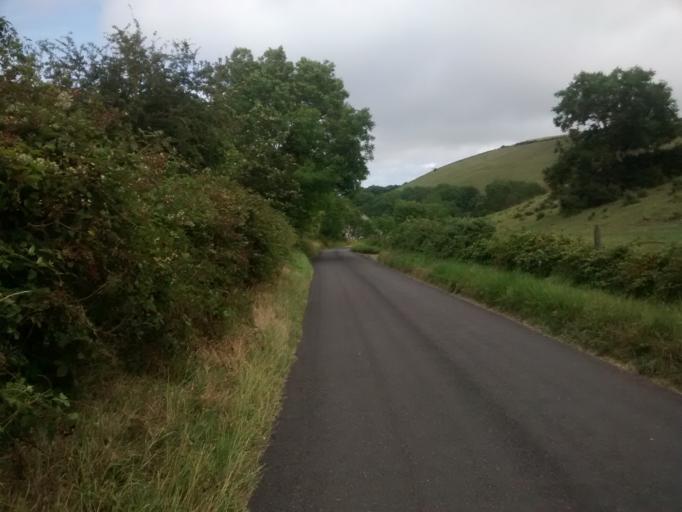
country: GB
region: England
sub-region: Dorset
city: Wareham
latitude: 50.6391
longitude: -2.1011
